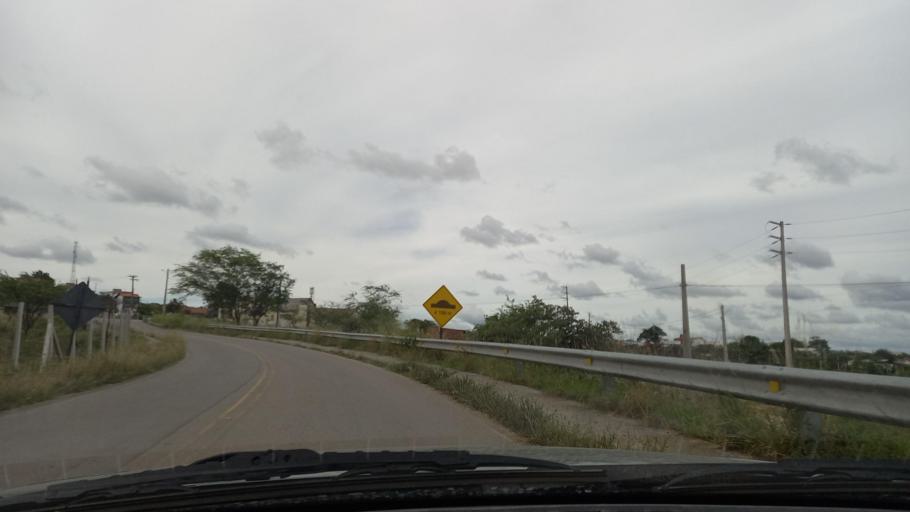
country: BR
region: Pernambuco
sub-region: Gravata
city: Gravata
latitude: -8.2259
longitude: -35.5808
